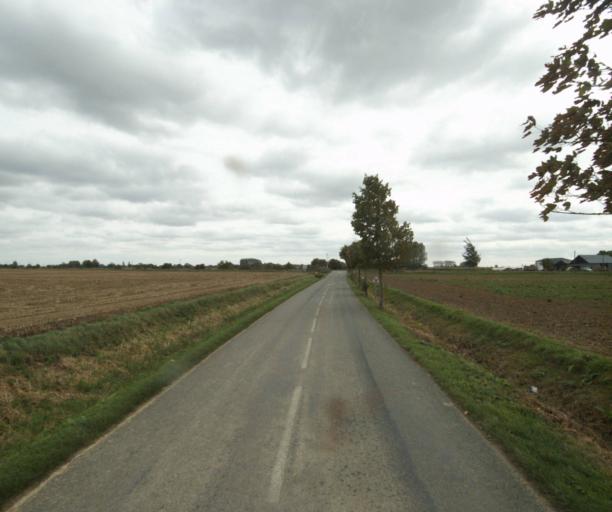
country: FR
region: Nord-Pas-de-Calais
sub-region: Departement du Pas-de-Calais
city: Fleurbaix
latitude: 50.6655
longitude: 2.8154
